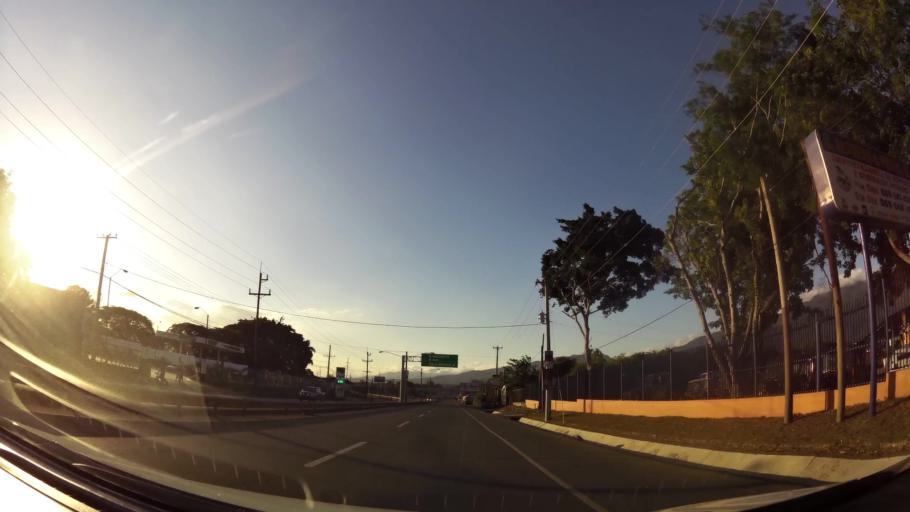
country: DO
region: Santiago
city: Palmar Arriba
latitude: 19.5147
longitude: -70.7610
